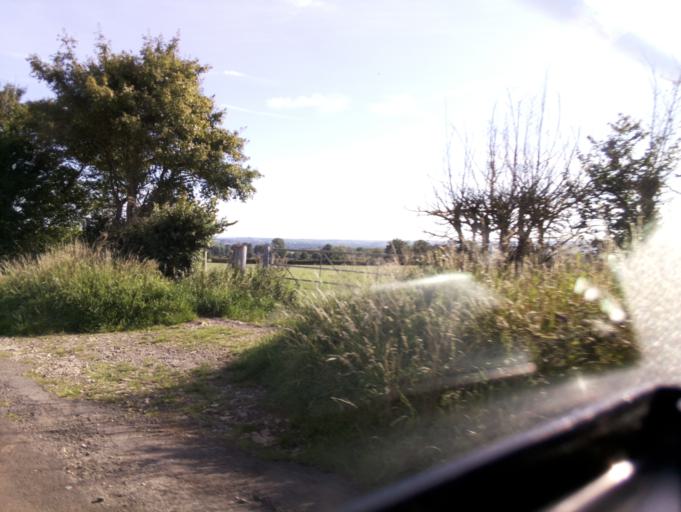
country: GB
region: England
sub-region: Bath and North East Somerset
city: Publow
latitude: 51.3928
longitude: -2.5328
